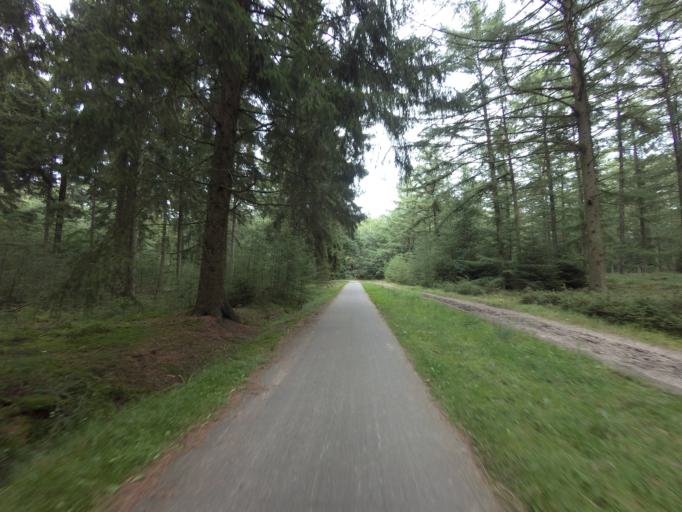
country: NL
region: Drenthe
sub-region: Gemeente Westerveld
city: Dwingeloo
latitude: 52.8944
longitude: 6.2946
